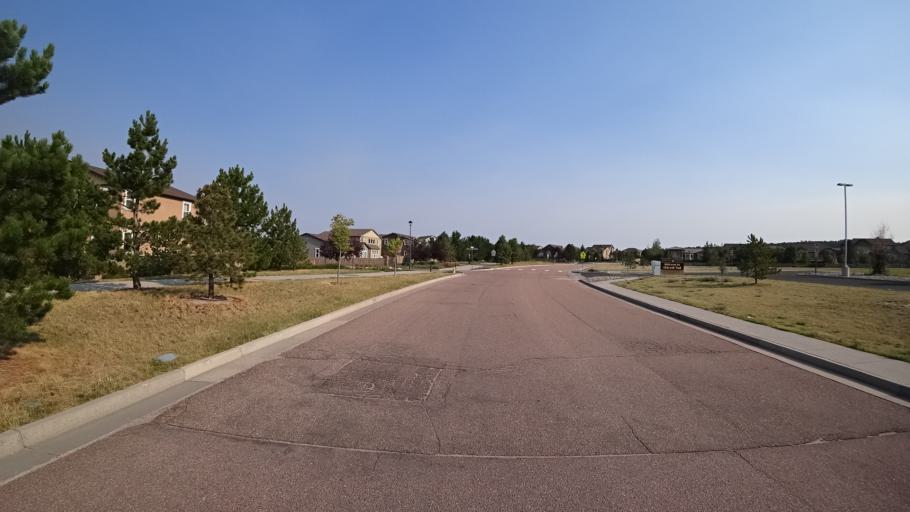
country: US
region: Colorado
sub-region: El Paso County
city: Black Forest
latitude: 38.9744
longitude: -104.7367
